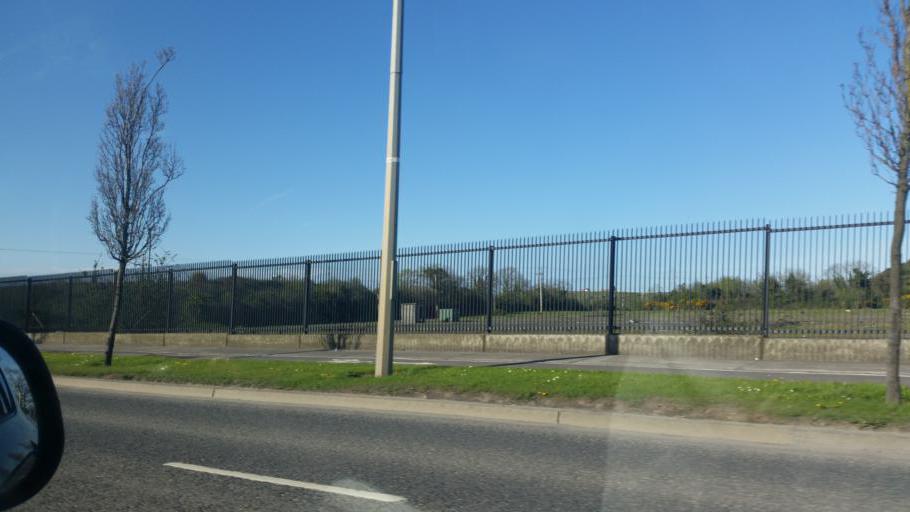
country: IE
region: Leinster
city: Castleknock
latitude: 53.4007
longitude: -6.3349
